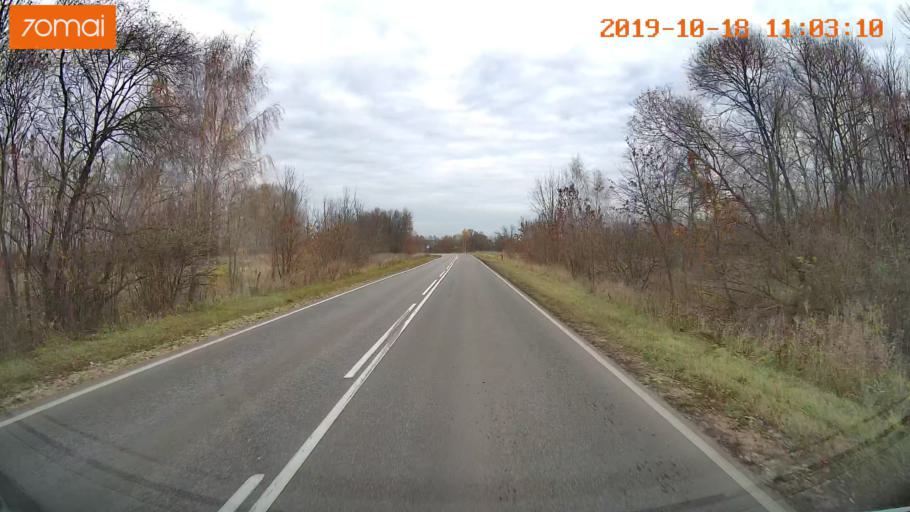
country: RU
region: Tula
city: Yepifan'
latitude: 53.8758
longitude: 38.5471
